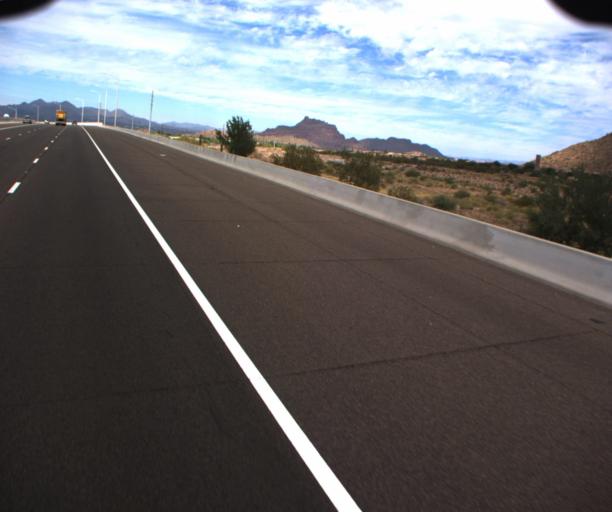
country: US
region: Arizona
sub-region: Pinal County
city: Apache Junction
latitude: 33.4692
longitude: -111.6809
